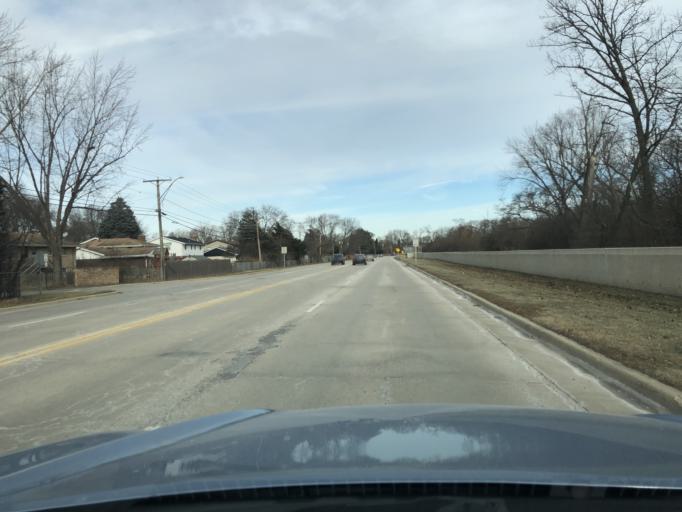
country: US
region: Illinois
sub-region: Cook County
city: Prospect Heights
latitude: 42.0976
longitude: -87.8904
